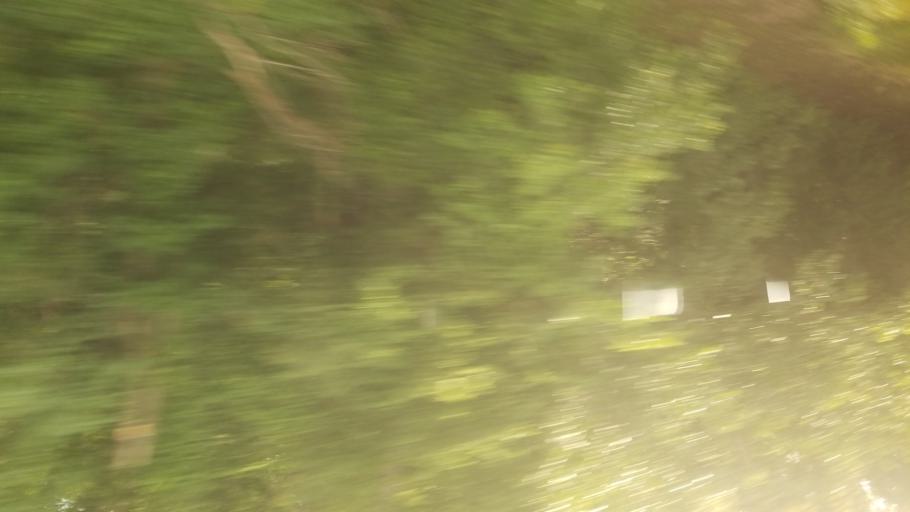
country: US
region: Kansas
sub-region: Johnson County
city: De Soto
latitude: 38.9779
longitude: -95.0177
